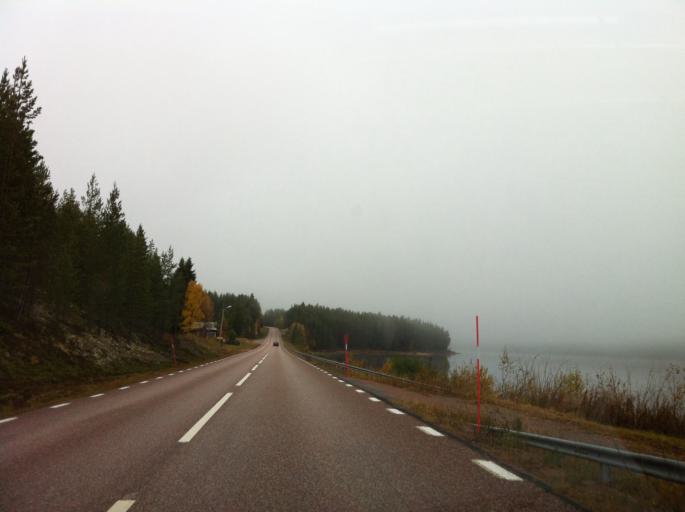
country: NO
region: Hedmark
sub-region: Trysil
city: Innbygda
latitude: 61.7404
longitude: 12.9780
